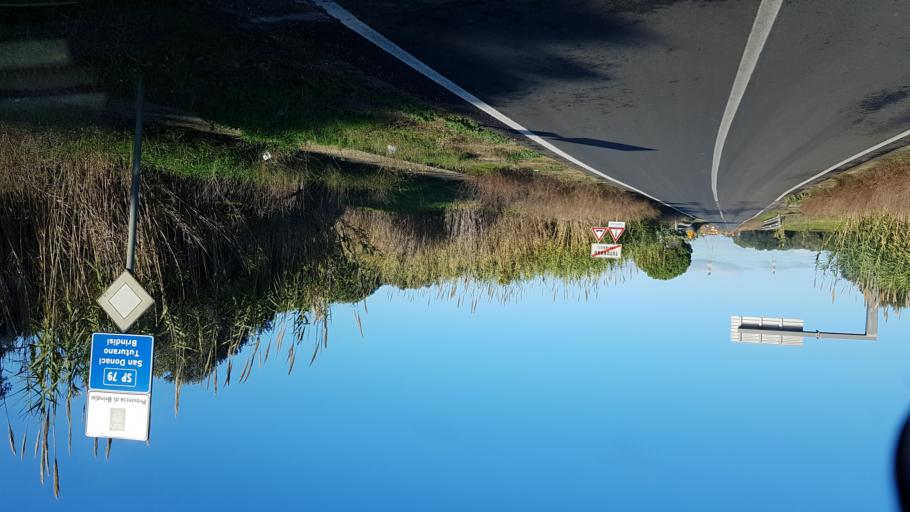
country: IT
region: Apulia
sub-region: Provincia di Brindisi
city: Tuturano
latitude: 40.5494
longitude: 17.9475
